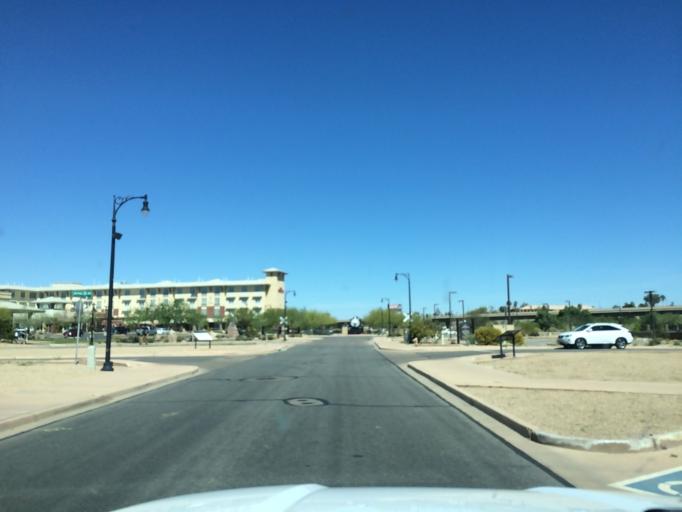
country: US
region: Arizona
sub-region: Yuma County
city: Yuma
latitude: 32.7261
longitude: -114.6197
